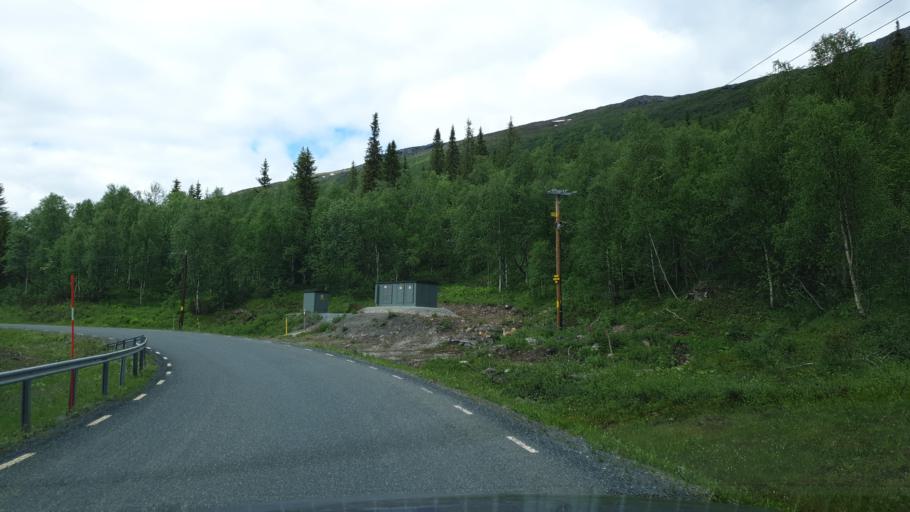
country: NO
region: Nordland
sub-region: Hattfjelldal
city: Hattfjelldal
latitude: 65.4280
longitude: 14.6010
